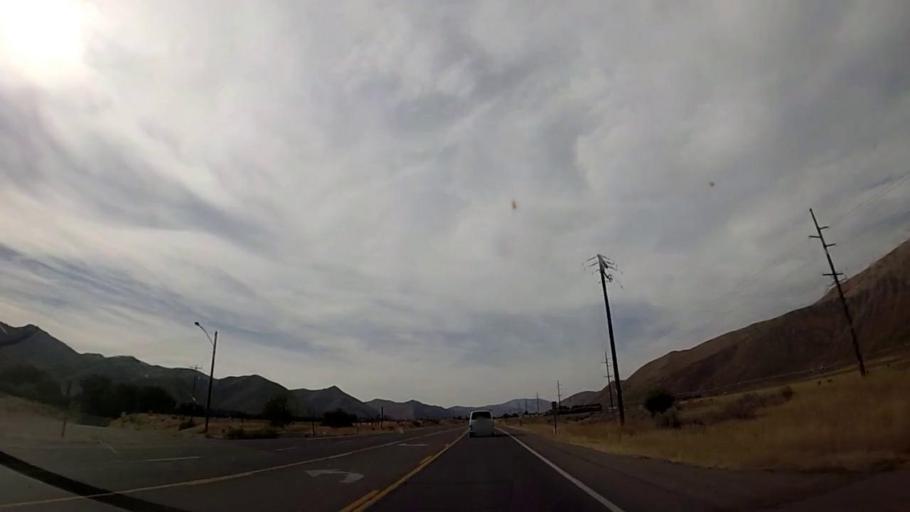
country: US
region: Idaho
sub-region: Blaine County
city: Bellevue
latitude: 43.4769
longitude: -114.2677
